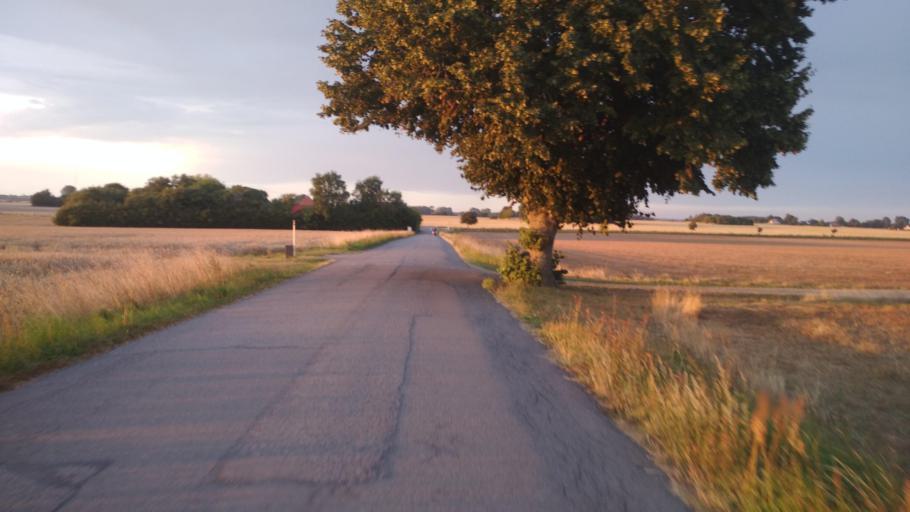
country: DK
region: Capital Region
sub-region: Bornholm Kommune
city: Akirkeby
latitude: 55.0325
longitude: 14.9145
